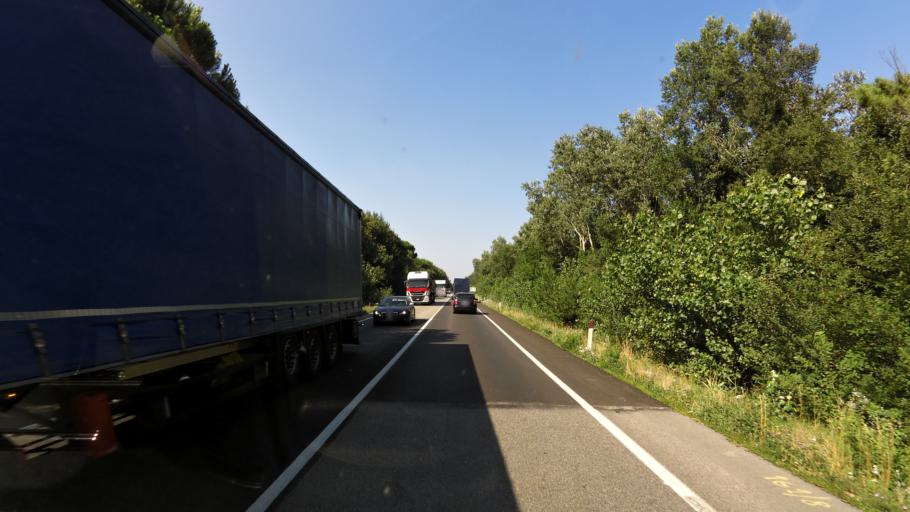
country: IT
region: Emilia-Romagna
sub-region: Provincia di Ravenna
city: Marina Romea
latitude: 44.4900
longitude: 12.2142
